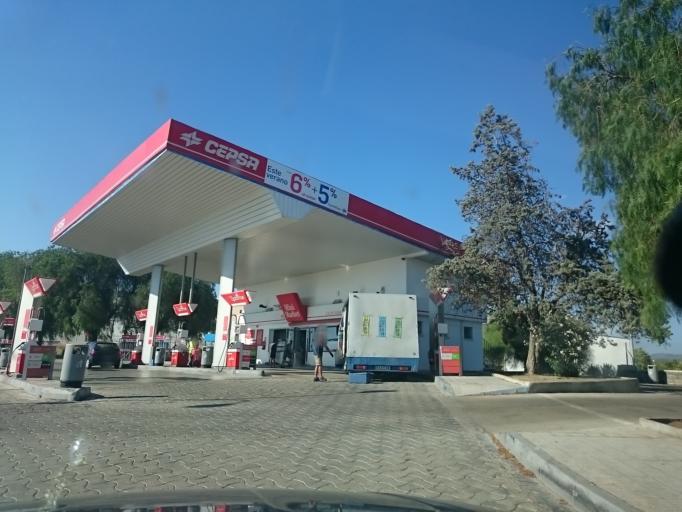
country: ES
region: Catalonia
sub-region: Provincia de Barcelona
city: Vilanova i la Geltru
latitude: 41.2388
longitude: 1.7261
